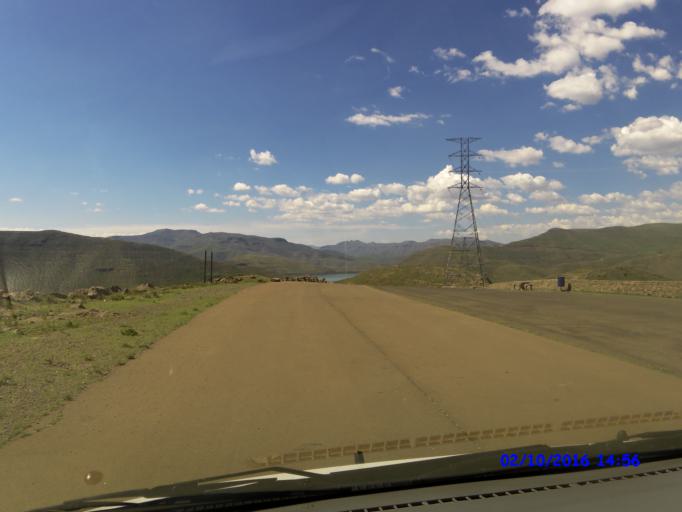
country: LS
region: Maseru
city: Nako
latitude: -29.4706
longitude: 28.0895
